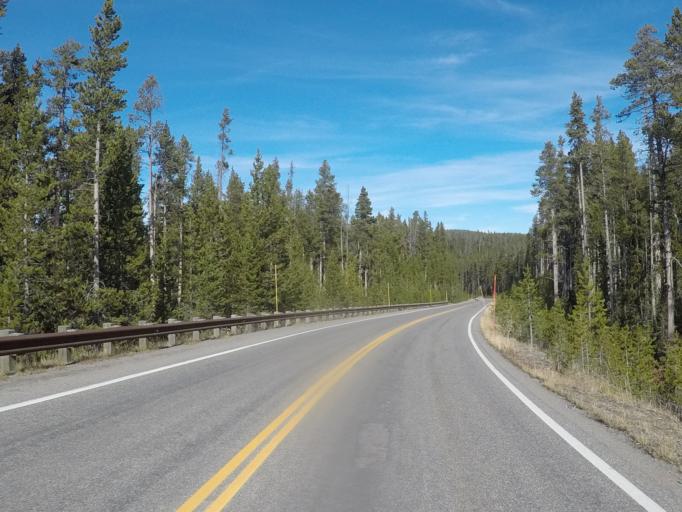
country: US
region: Montana
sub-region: Gallatin County
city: West Yellowstone
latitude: 44.4447
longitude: -110.6780
